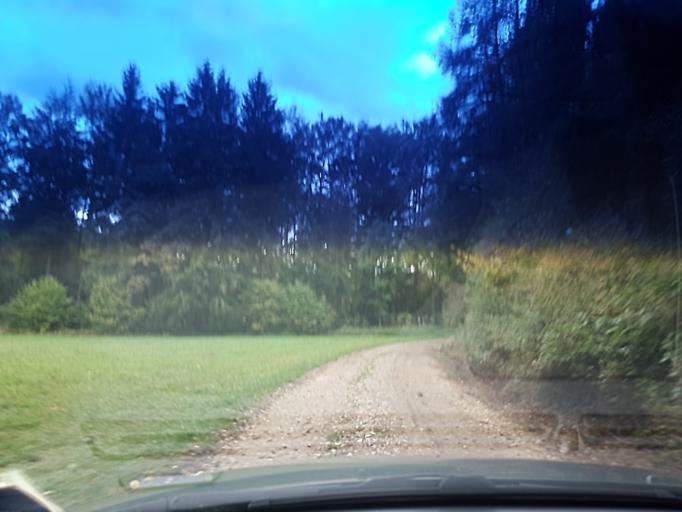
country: DE
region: Bavaria
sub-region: Upper Franconia
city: Wattendorf
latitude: 49.9894
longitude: 11.0950
